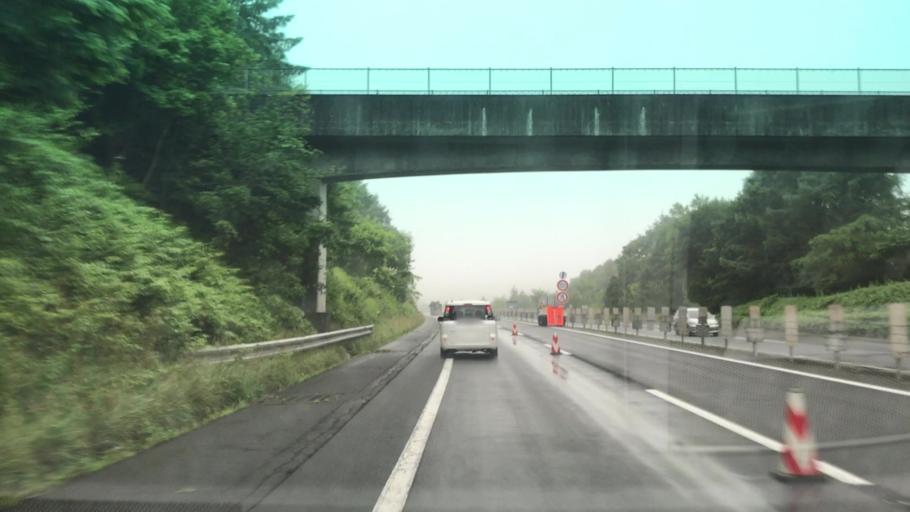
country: JP
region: Hokkaido
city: Tomakomai
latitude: 42.6619
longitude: 141.5820
